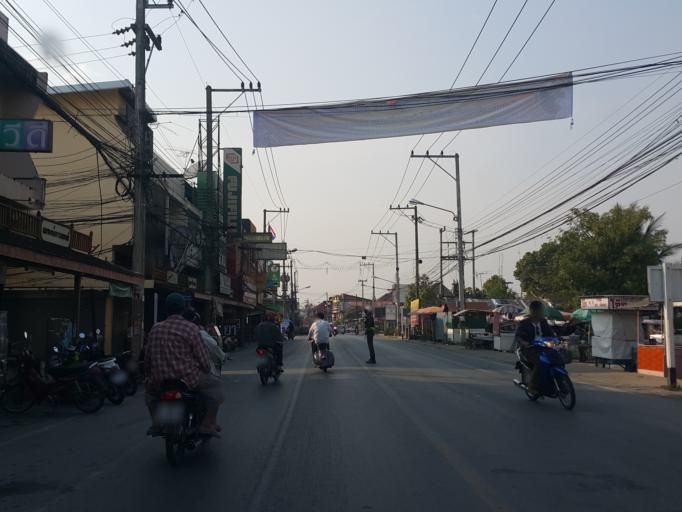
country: TH
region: Chiang Mai
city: San Kamphaeng
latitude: 18.7443
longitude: 99.1205
